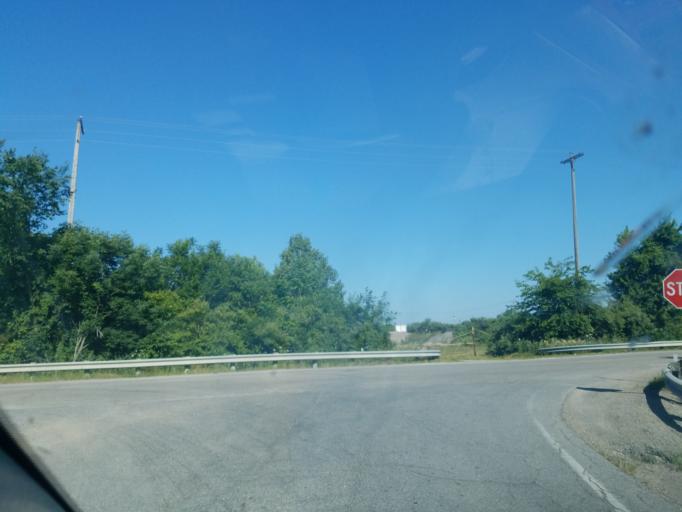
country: US
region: Ohio
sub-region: Union County
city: Richwood
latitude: 40.4149
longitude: -83.4527
